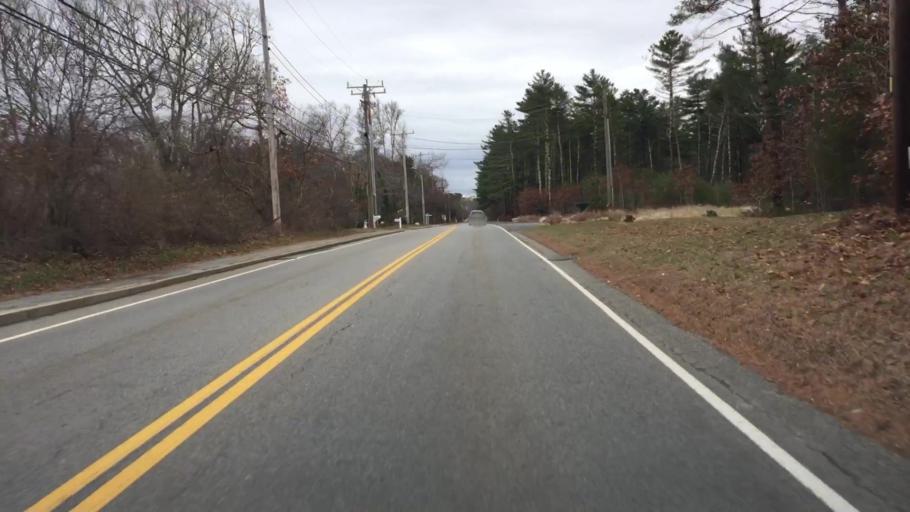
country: US
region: Massachusetts
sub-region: Barnstable County
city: Teaticket
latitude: 41.5790
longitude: -70.6043
